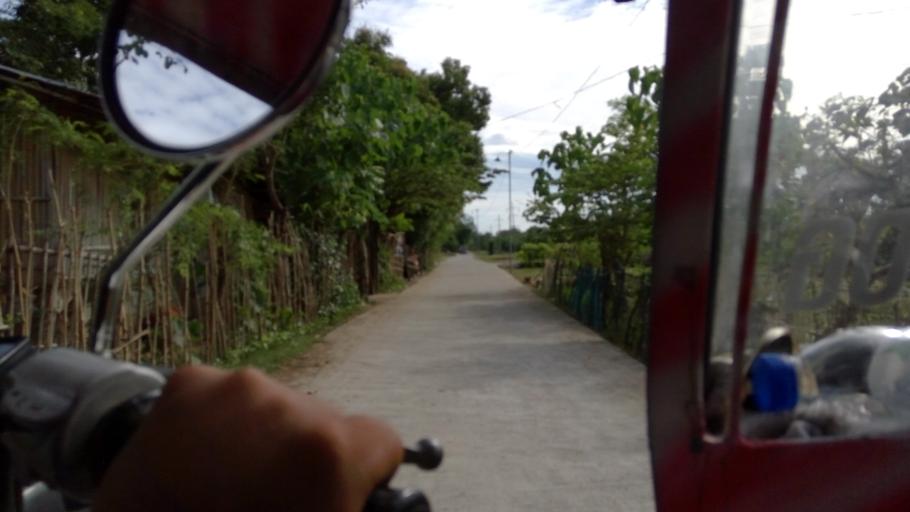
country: PH
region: Ilocos
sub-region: Province of La Union
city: San Eugenio
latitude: 16.3698
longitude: 120.3524
